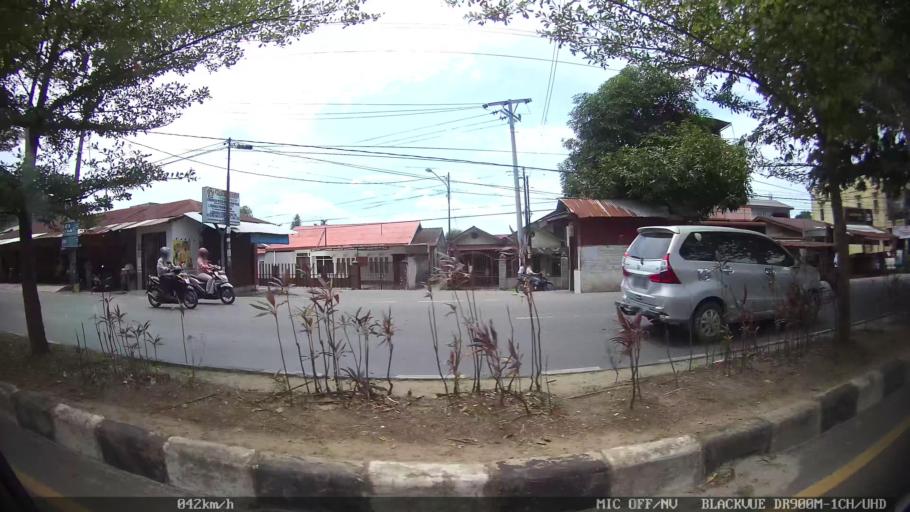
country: ID
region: North Sumatra
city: Deli Tua
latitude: 3.5332
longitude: 98.6472
